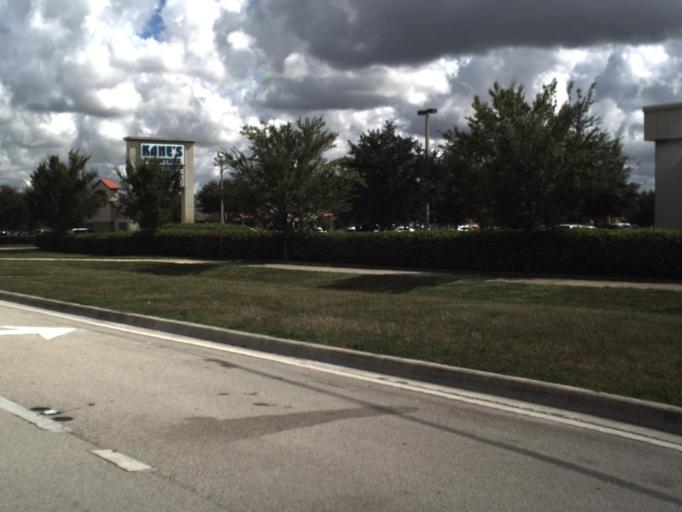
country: US
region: Florida
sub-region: Polk County
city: Gibsonia
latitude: 28.1017
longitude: -81.9736
